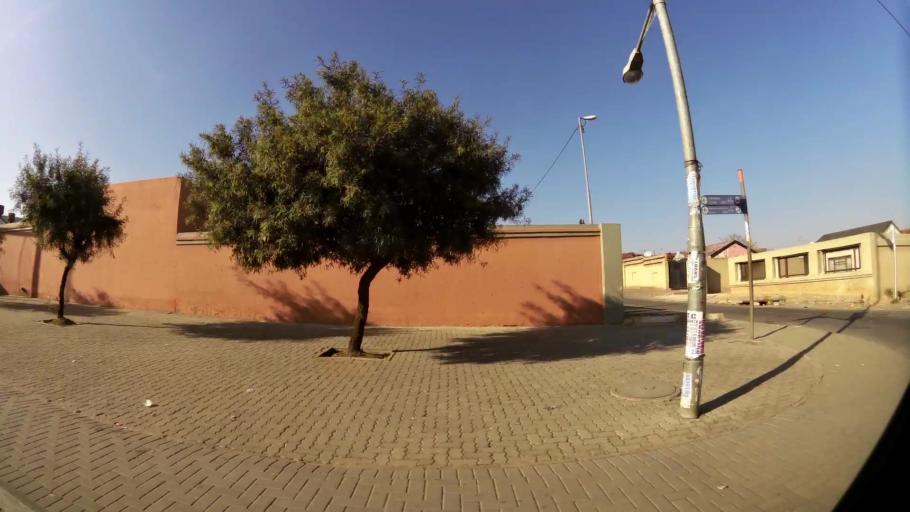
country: ZA
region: Gauteng
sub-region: City of Johannesburg Metropolitan Municipality
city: Soweto
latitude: -26.2279
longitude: 27.9306
